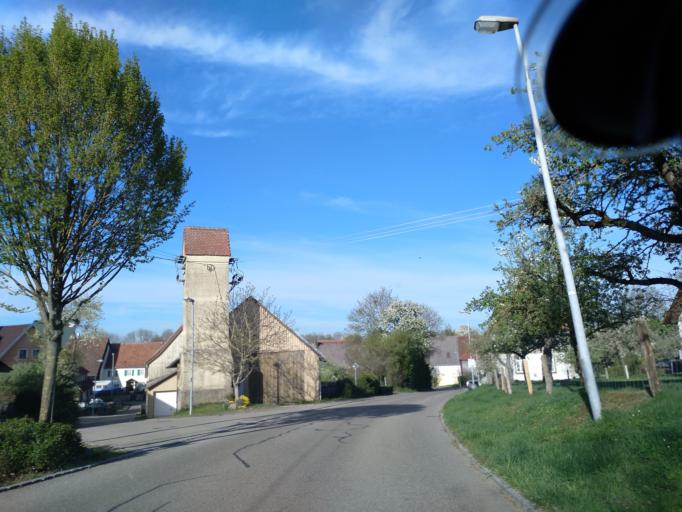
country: DE
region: Baden-Wuerttemberg
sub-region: Regierungsbezirk Stuttgart
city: Langenburg
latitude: 49.2254
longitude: 9.8448
